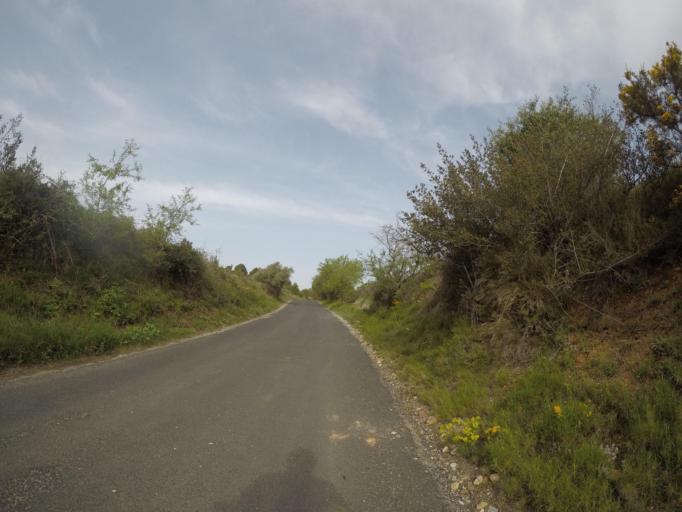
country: FR
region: Languedoc-Roussillon
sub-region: Departement des Pyrenees-Orientales
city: Baixas
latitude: 42.7688
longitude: 2.8087
